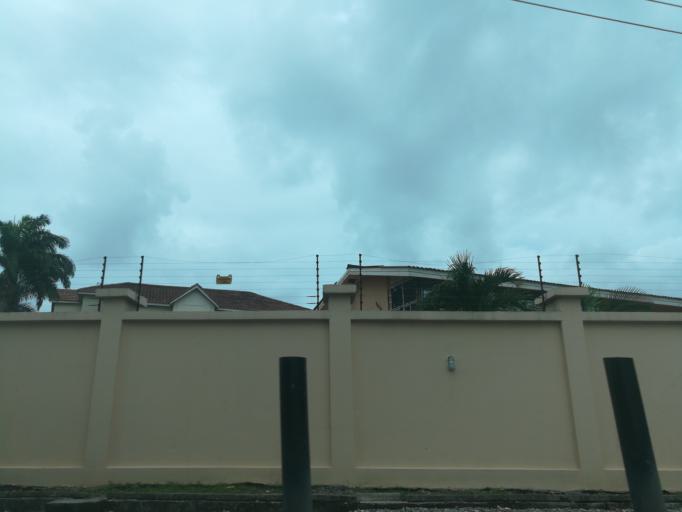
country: NG
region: Lagos
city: Ikoyi
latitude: 6.4329
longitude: 3.4231
